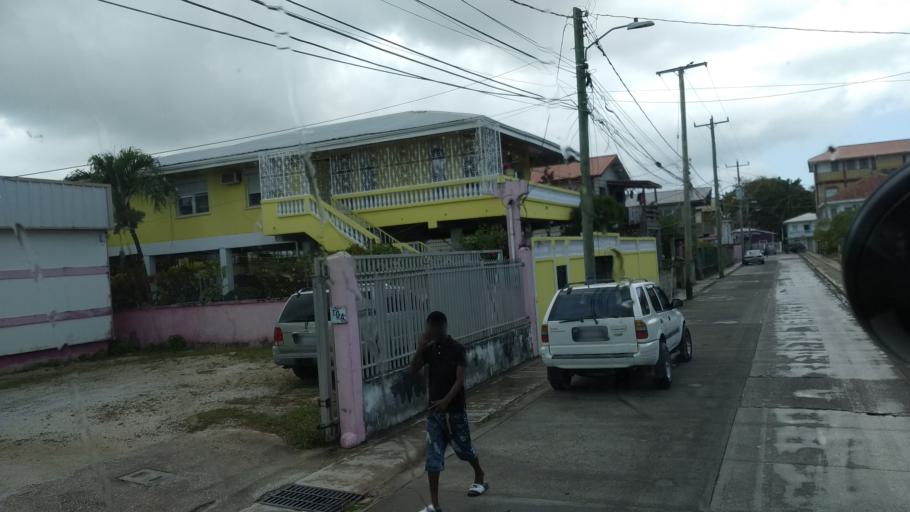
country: BZ
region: Belize
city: Belize City
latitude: 17.5003
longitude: -88.1896
